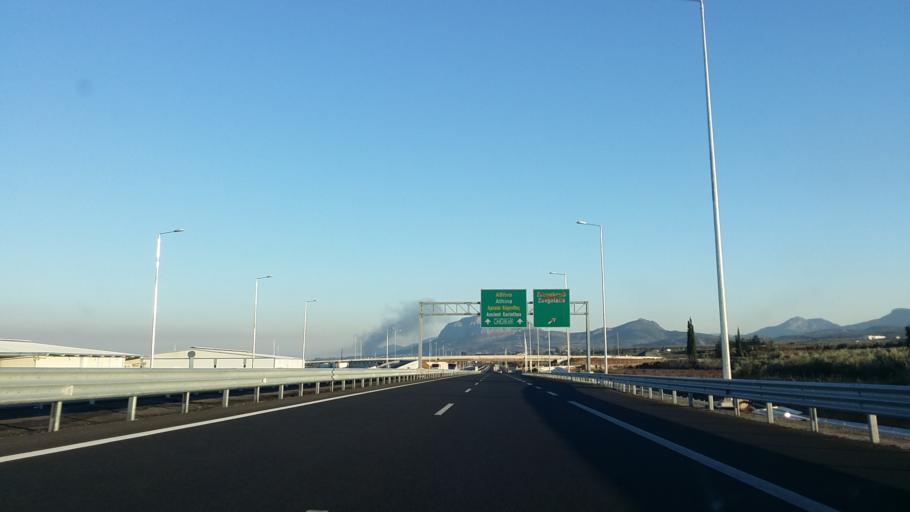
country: GR
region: Peloponnese
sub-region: Nomos Korinthias
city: Zevgolateio
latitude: 37.9308
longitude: 22.7852
